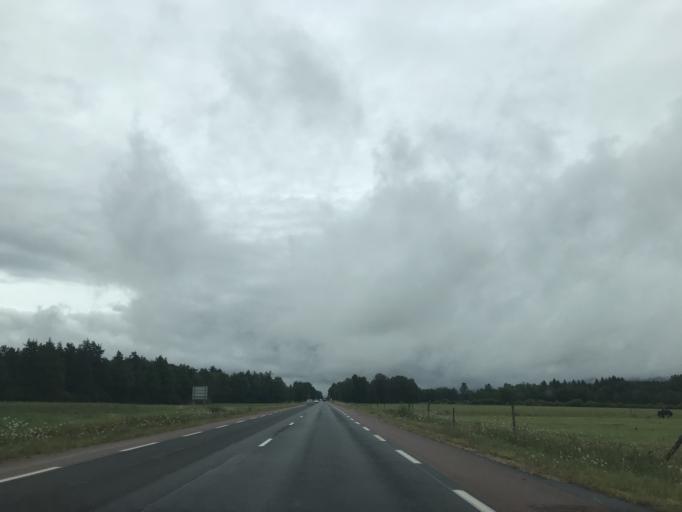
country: FR
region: Auvergne
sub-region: Departement du Puy-de-Dome
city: Arlanc
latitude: 45.4450
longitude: 3.7241
